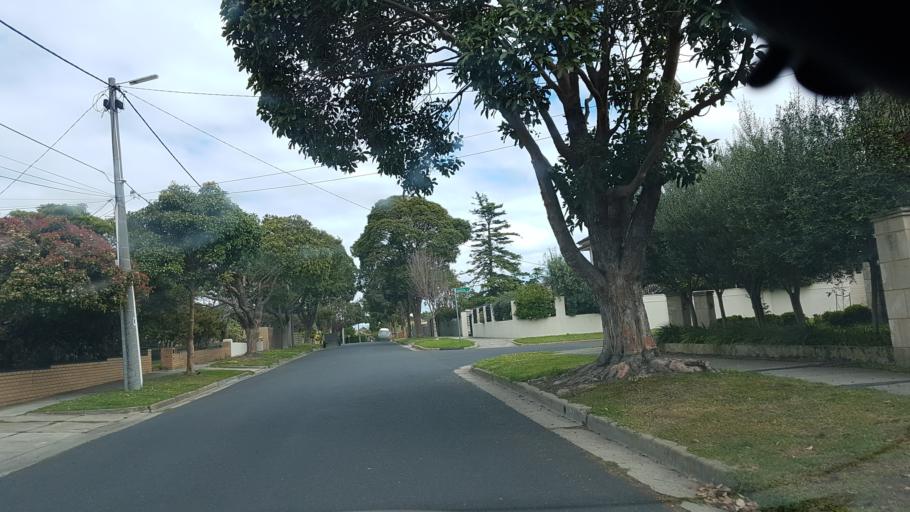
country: AU
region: Victoria
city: McKinnon
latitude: -37.9250
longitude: 145.0448
